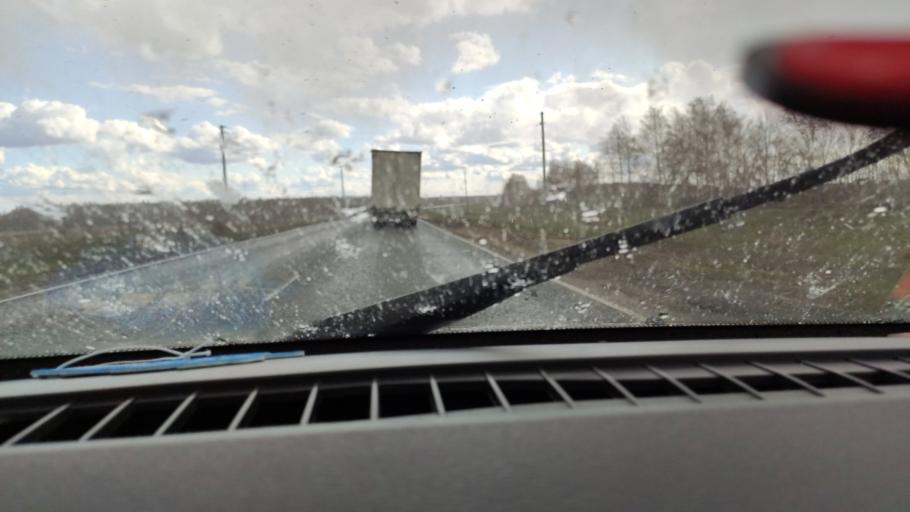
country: RU
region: Saratov
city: Balakovo
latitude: 52.1117
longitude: 47.7491
